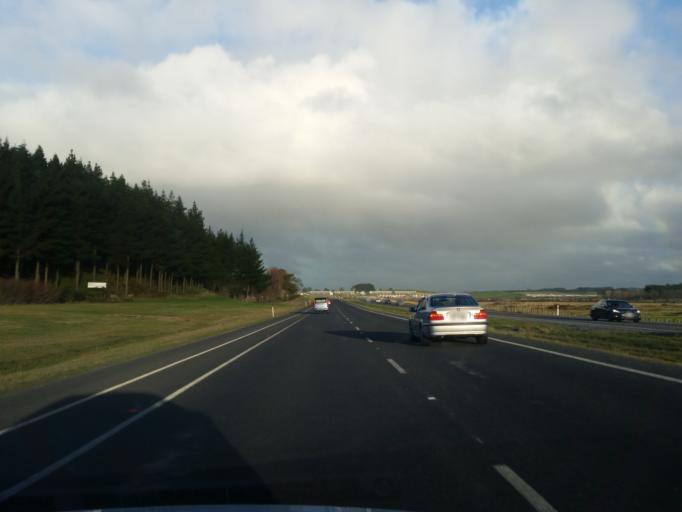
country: NZ
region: Waikato
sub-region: Waikato District
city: Te Kauwhata
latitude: -37.3414
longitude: 175.0655
